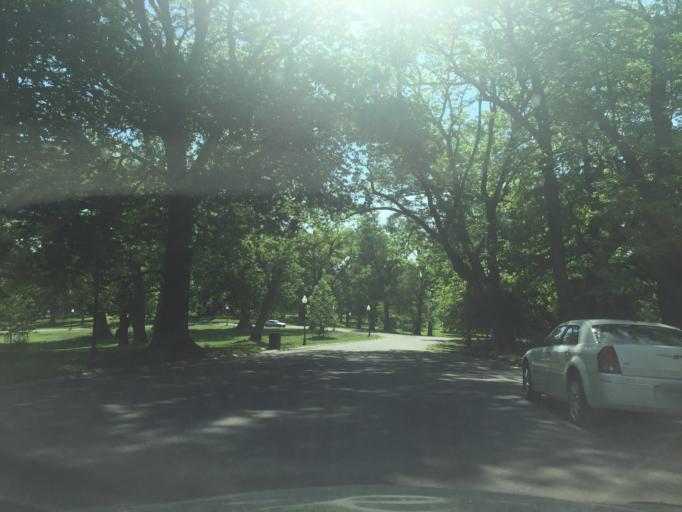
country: US
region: Maryland
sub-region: City of Baltimore
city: Baltimore
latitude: 39.3209
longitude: -76.6447
